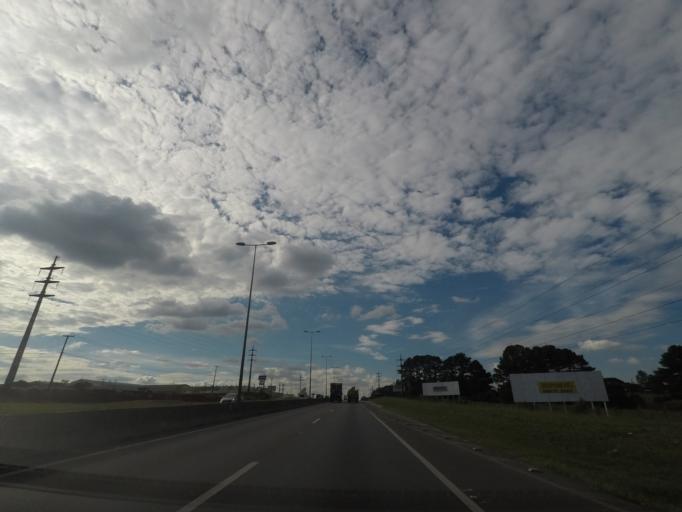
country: BR
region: Parana
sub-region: Araucaria
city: Araucaria
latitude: -25.5878
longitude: -49.3146
